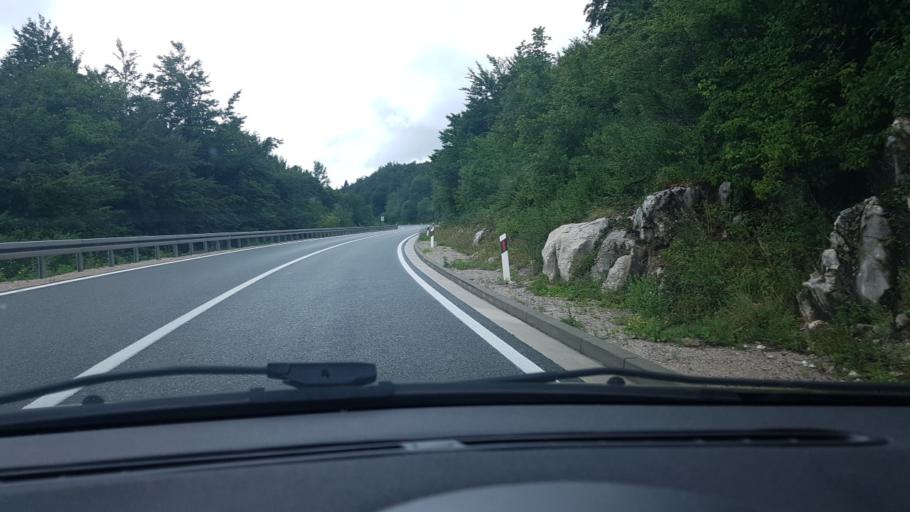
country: HR
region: Licko-Senjska
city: Jezerce
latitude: 44.8635
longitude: 15.6997
